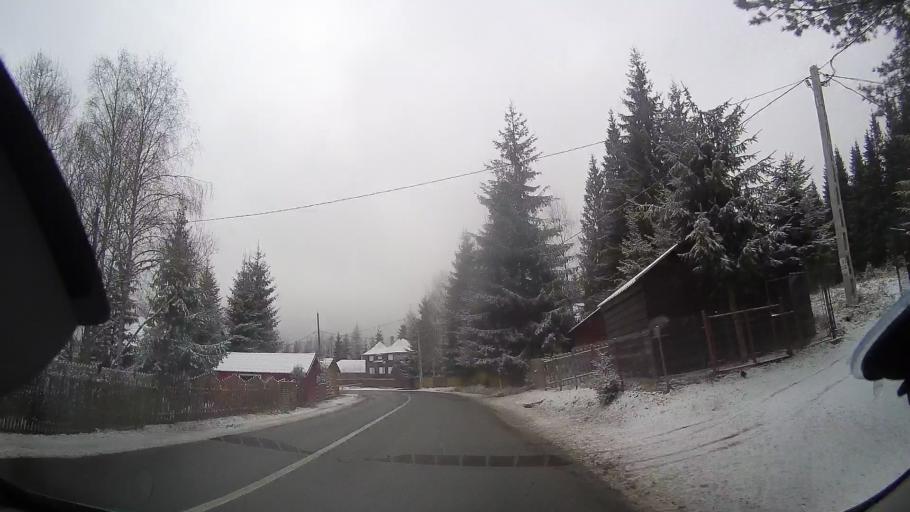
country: RO
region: Cluj
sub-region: Comuna Belis
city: Belis
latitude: 46.6813
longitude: 23.0362
